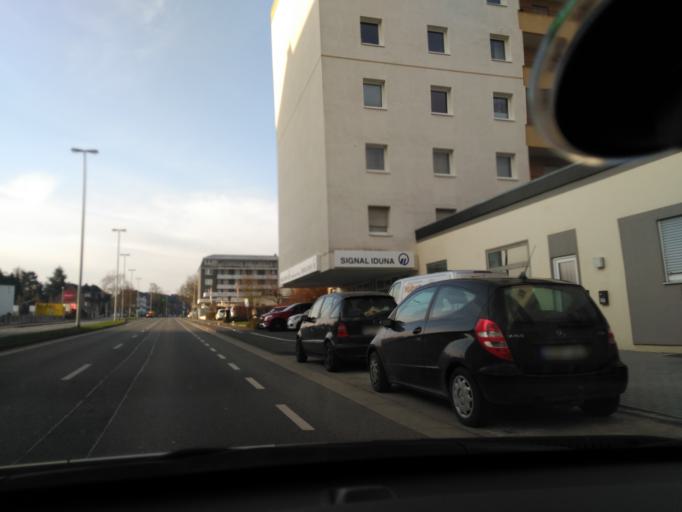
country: DE
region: North Rhine-Westphalia
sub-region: Regierungsbezirk Dusseldorf
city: Monchengladbach
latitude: 51.1653
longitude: 6.4254
